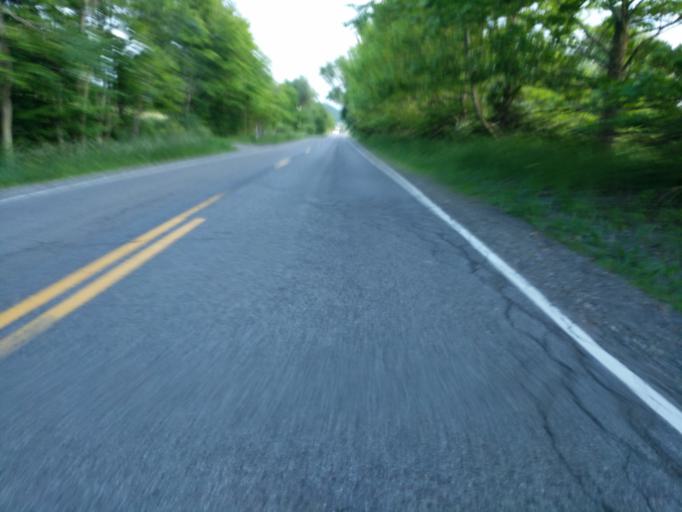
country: US
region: New York
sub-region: Tompkins County
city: Dryden
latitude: 42.4062
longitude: -76.3507
